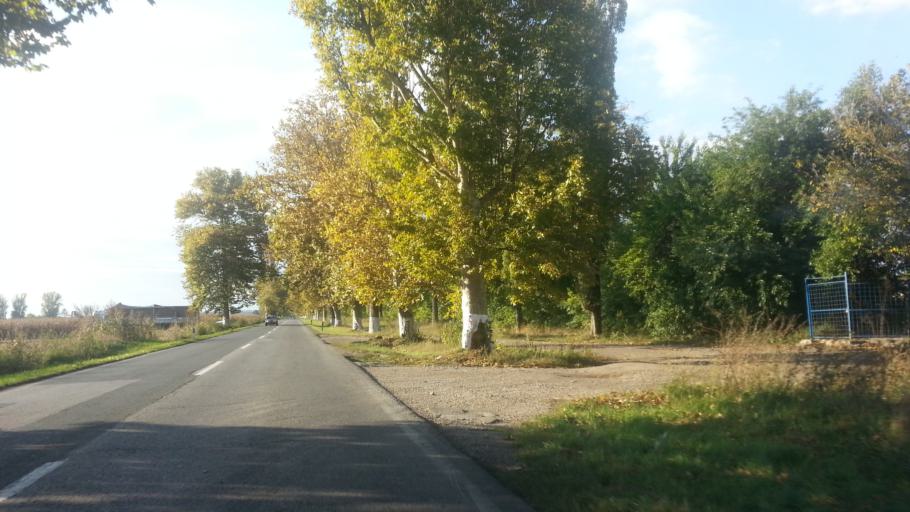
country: RS
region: Autonomna Pokrajina Vojvodina
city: Nova Pazova
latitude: 44.9291
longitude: 20.2415
